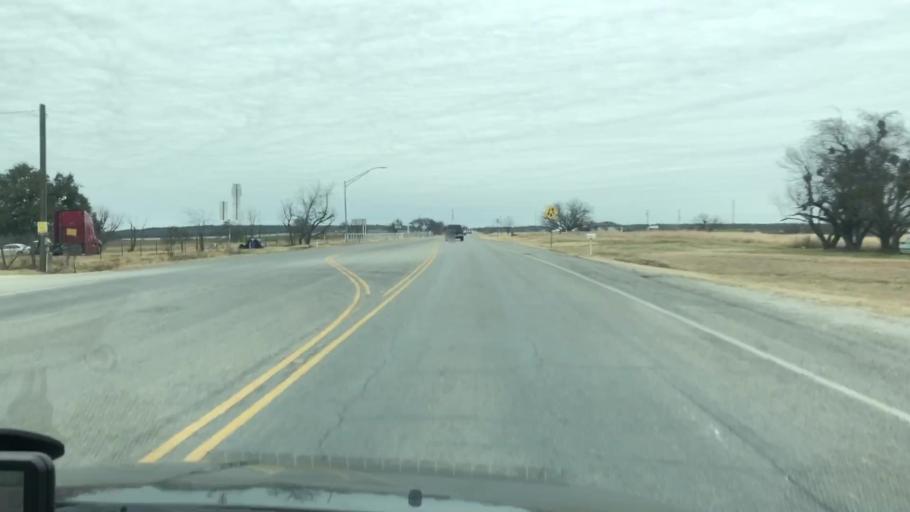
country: US
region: Texas
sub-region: Palo Pinto County
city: Mineral Wells
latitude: 32.9205
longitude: -98.0749
